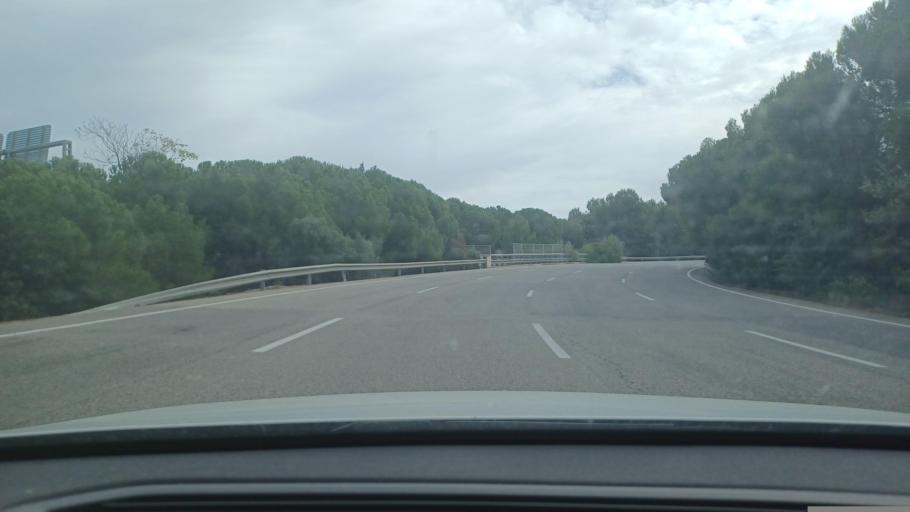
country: ES
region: Catalonia
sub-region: Provincia de Tarragona
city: Vila-seca
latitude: 41.1015
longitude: 1.1547
